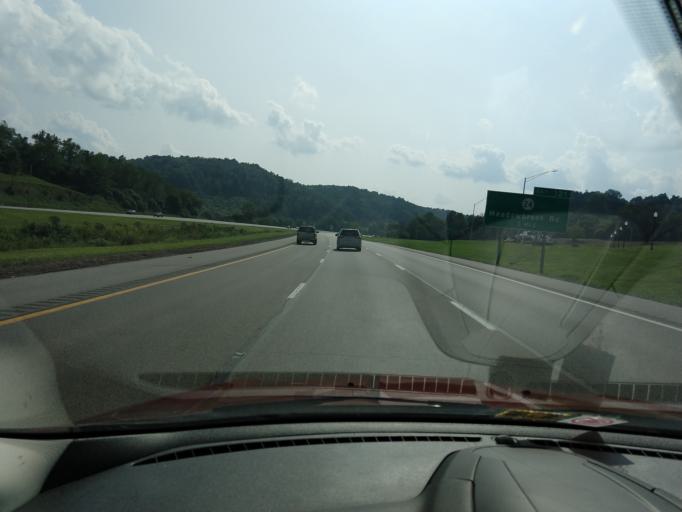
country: US
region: West Virginia
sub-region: Harrison County
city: Bridgeport
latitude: 39.3142
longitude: -80.2532
